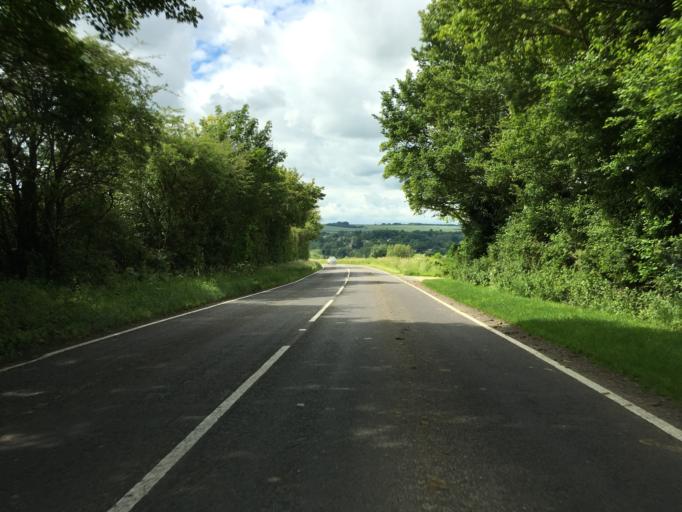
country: GB
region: England
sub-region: Oxfordshire
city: Shipton under Wychwood
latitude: 51.8695
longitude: -1.5876
